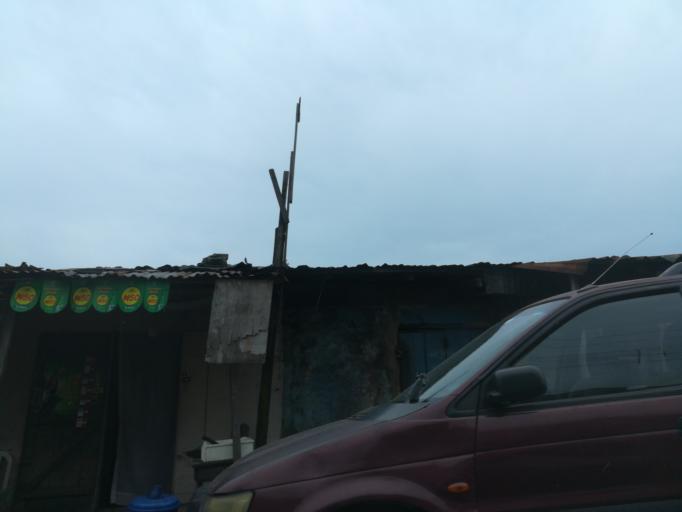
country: NG
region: Lagos
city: Makoko
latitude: 6.5015
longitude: 3.3895
